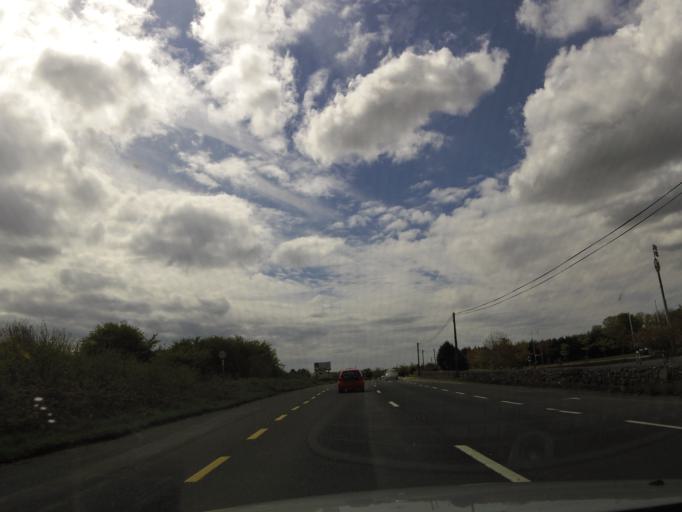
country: IE
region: Connaught
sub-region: County Galway
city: Claregalway
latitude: 53.3170
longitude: -8.9811
